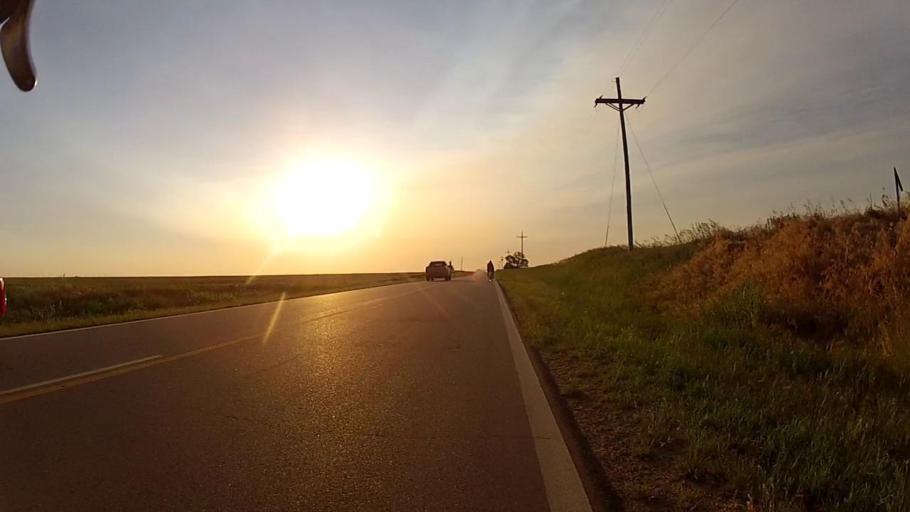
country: US
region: Kansas
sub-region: Harper County
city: Anthony
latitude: 37.1526
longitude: -97.9478
